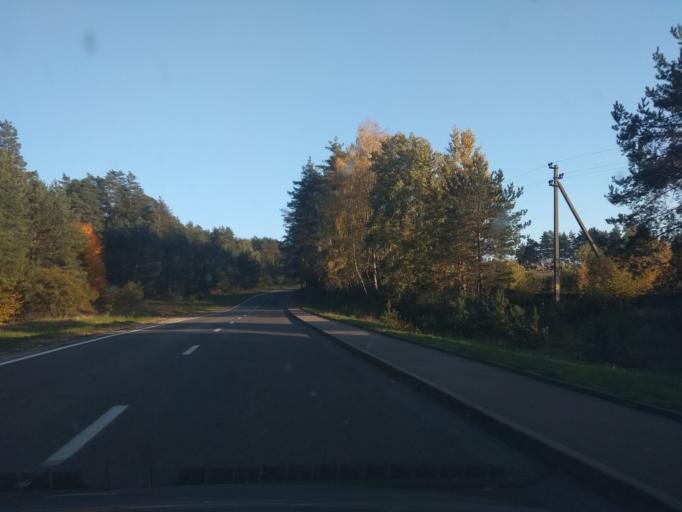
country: BY
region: Grodnenskaya
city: Vawkavysk
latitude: 53.1548
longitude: 24.4941
